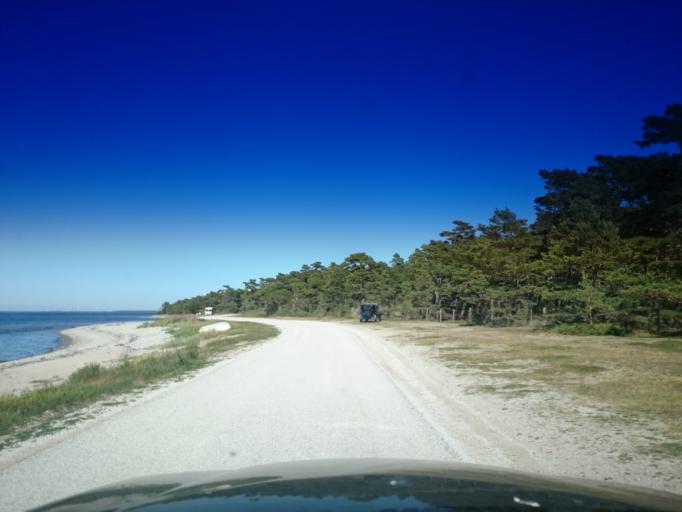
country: SE
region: Gotland
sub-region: Gotland
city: Klintehamn
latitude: 57.2951
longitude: 18.1267
